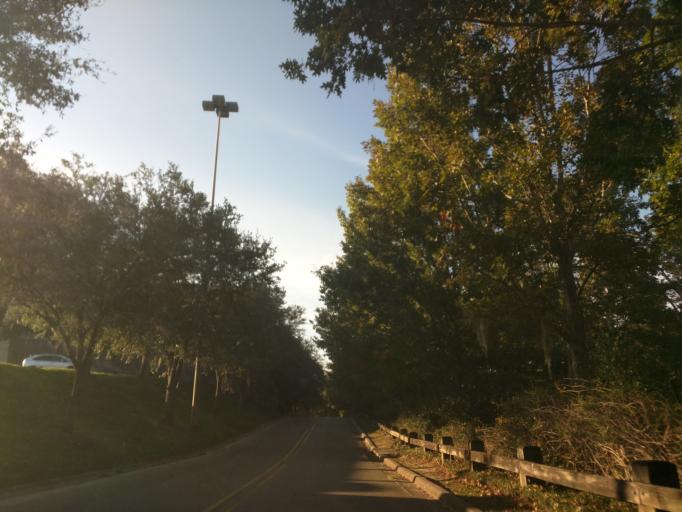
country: US
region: Florida
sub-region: Leon County
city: Tallahassee
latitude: 30.4378
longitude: -84.2516
